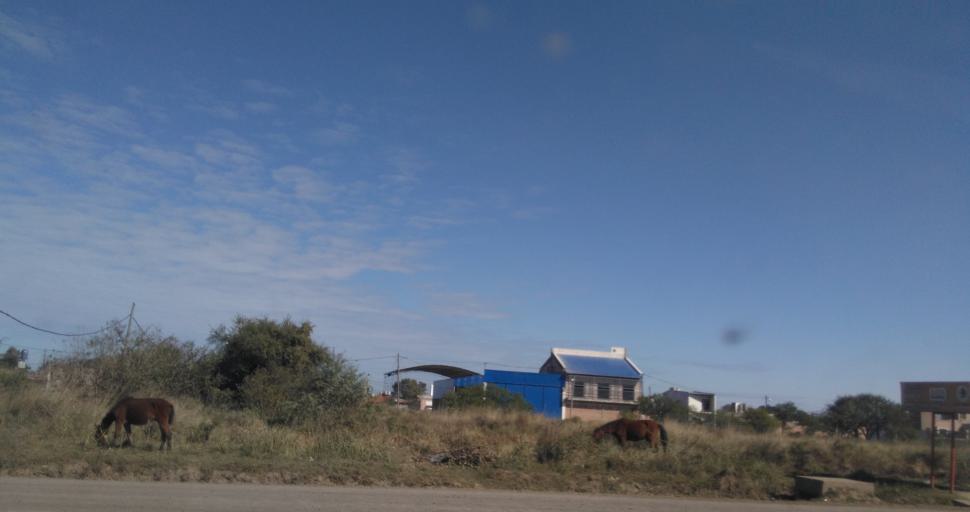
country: AR
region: Chaco
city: Fontana
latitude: -27.4587
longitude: -59.0432
